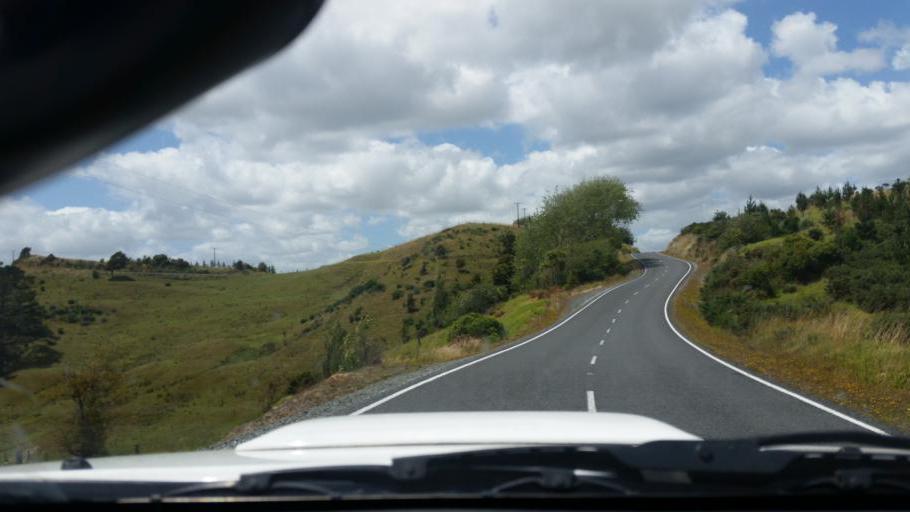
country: NZ
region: Northland
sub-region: Whangarei
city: Ruakaka
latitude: -36.0807
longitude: 174.2393
